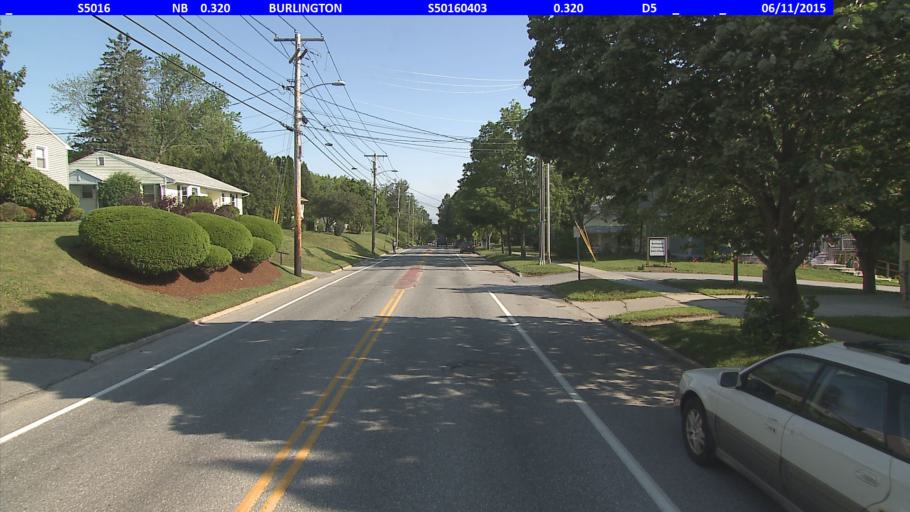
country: US
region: Vermont
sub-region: Chittenden County
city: Winooski
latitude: 44.4772
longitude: -73.1913
